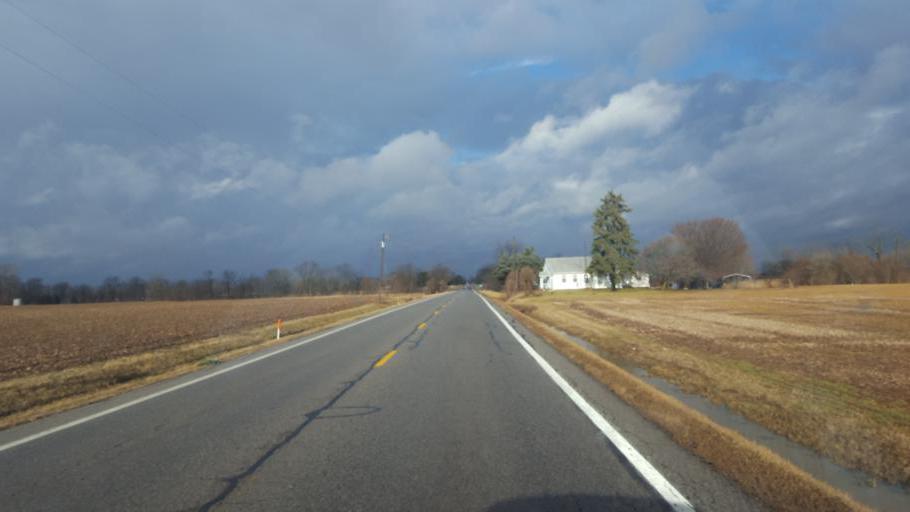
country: US
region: Ohio
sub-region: Morrow County
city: Mount Gilead
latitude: 40.5758
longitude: -82.8940
